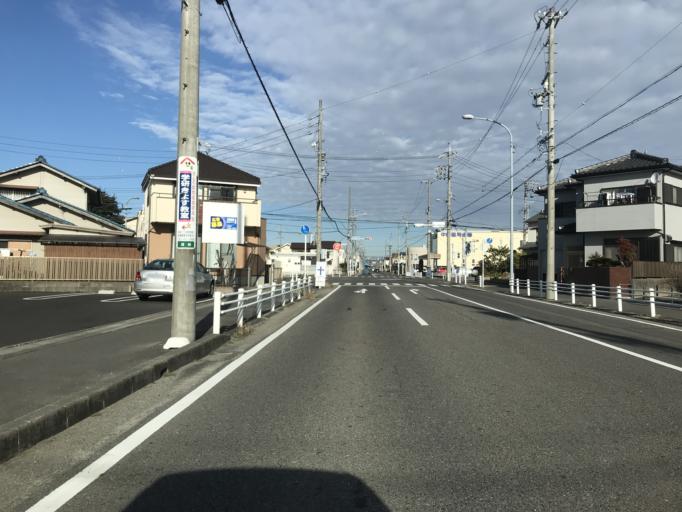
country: JP
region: Aichi
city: Inazawa
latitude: 35.2132
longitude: 136.8364
